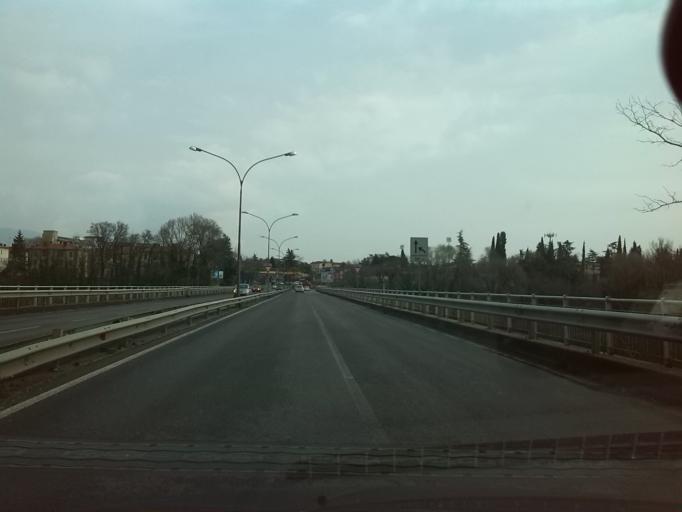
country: IT
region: Friuli Venezia Giulia
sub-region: Provincia di Gorizia
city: Gorizia
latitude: 45.9352
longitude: 13.5971
